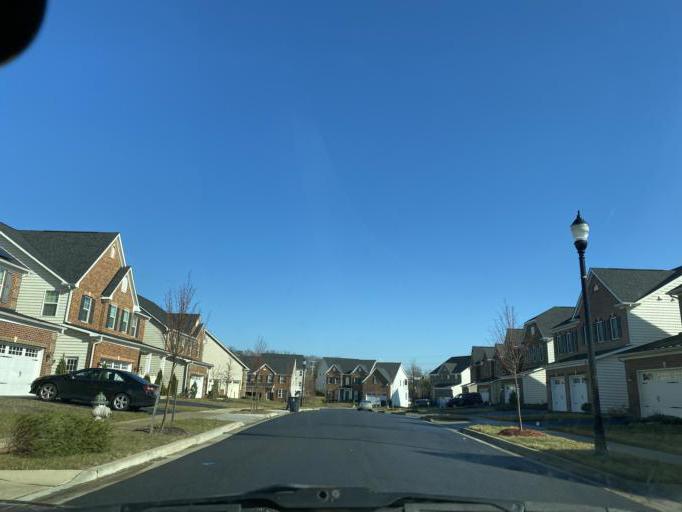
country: US
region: Maryland
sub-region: Prince George's County
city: West Laurel
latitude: 39.0885
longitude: -76.9168
